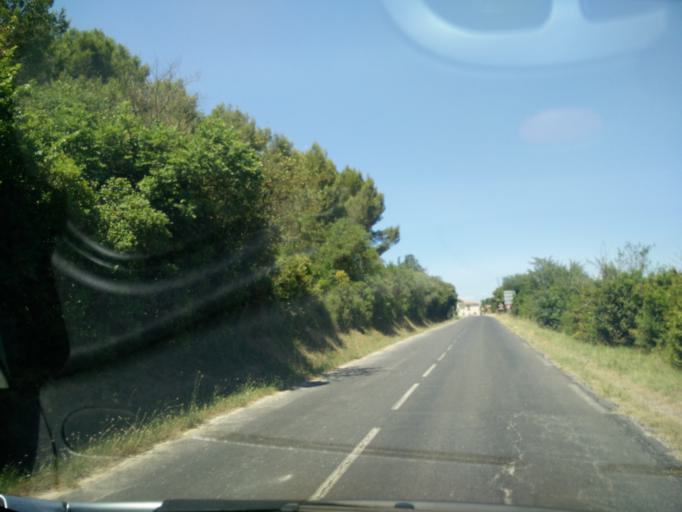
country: FR
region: Languedoc-Roussillon
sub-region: Departement de l'Herault
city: Villetelle
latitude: 43.7185
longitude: 4.1119
